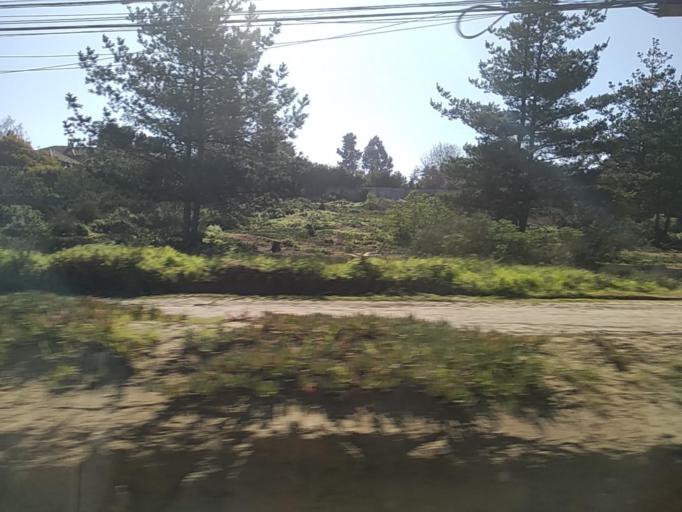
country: CL
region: Valparaiso
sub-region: Provincia de Valparaiso
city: Vina del Mar
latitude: -32.9598
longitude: -71.5312
